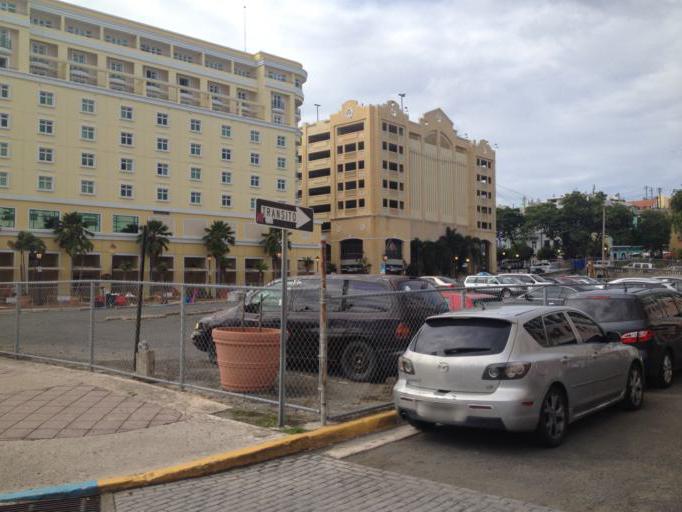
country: PR
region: San Juan
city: San Juan
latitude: 18.4641
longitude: -66.1114
